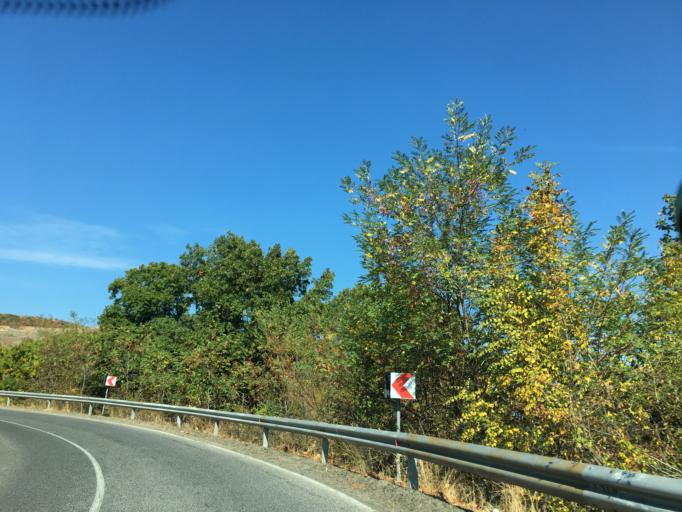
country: BG
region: Kurdzhali
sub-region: Obshtina Krumovgrad
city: Krumovgrad
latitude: 41.4788
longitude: 25.5536
